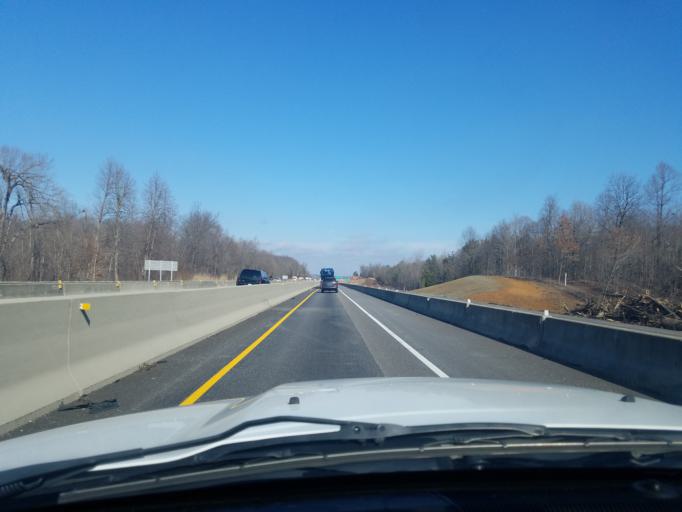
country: US
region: Kentucky
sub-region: Hardin County
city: Elizabethtown
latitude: 37.6590
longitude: -85.8549
